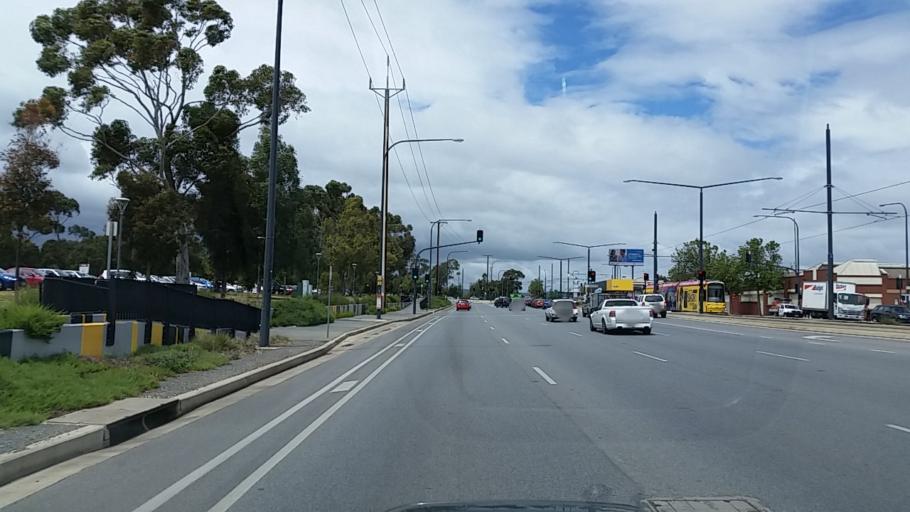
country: AU
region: South Australia
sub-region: City of West Torrens
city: Thebarton
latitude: -34.9164
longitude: 138.5785
